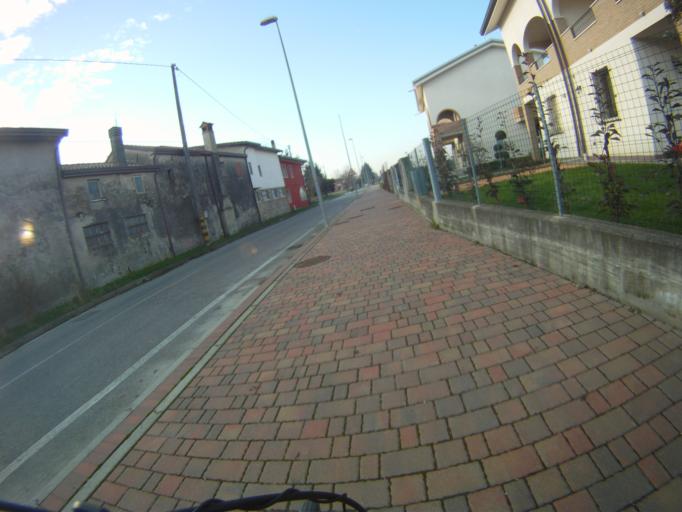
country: IT
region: Veneto
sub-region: Provincia di Padova
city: Polverara
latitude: 45.3113
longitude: 11.9545
